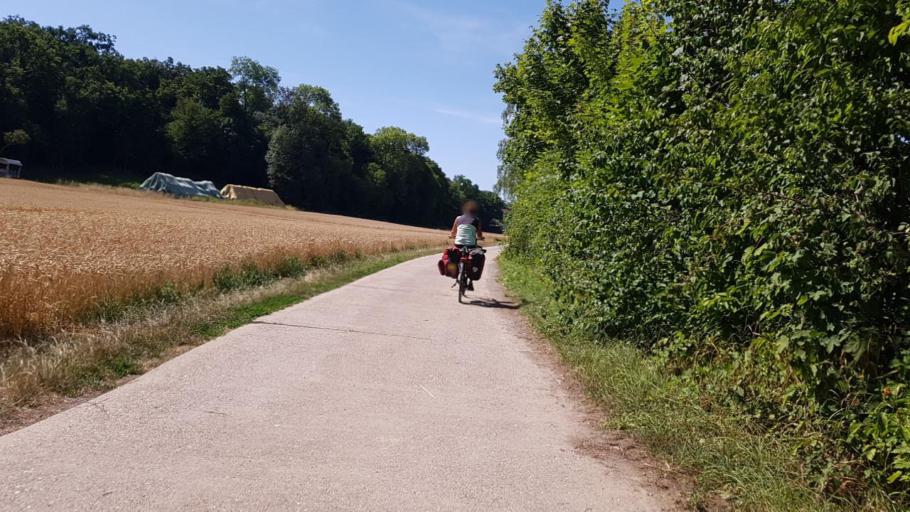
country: DE
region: Baden-Wuerttemberg
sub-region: Karlsruhe Region
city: Sulzfeld
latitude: 49.1437
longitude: 8.8664
